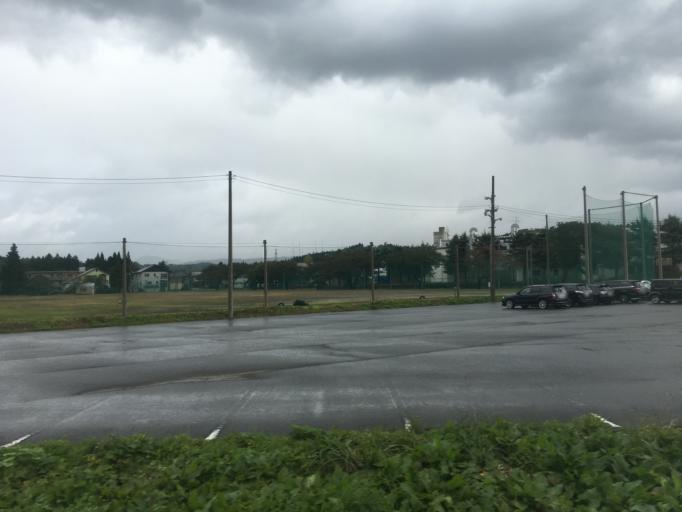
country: JP
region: Yamagata
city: Nagai
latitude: 38.0658
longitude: 139.7462
